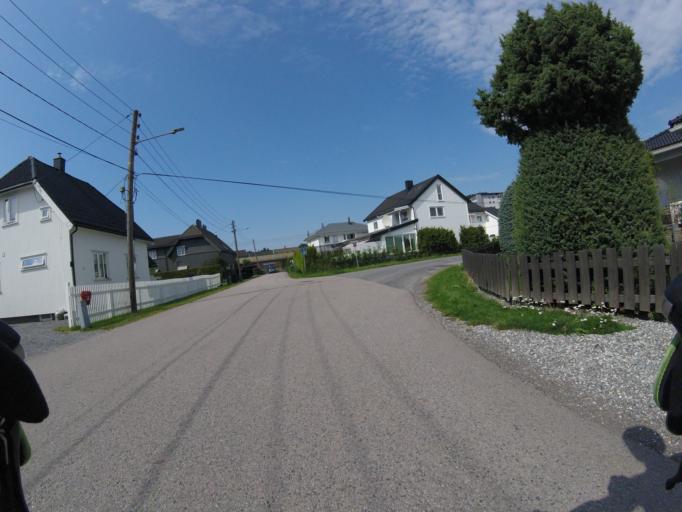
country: NO
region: Akershus
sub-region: Skedsmo
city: Lillestrom
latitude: 59.9573
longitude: 11.0601
